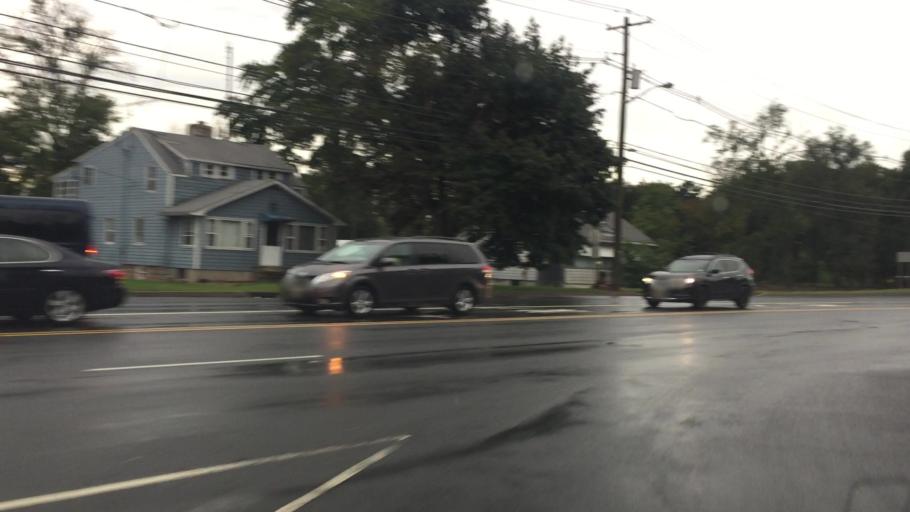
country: US
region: New Jersey
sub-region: Middlesex County
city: Society Hill
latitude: 40.5530
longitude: -74.4447
